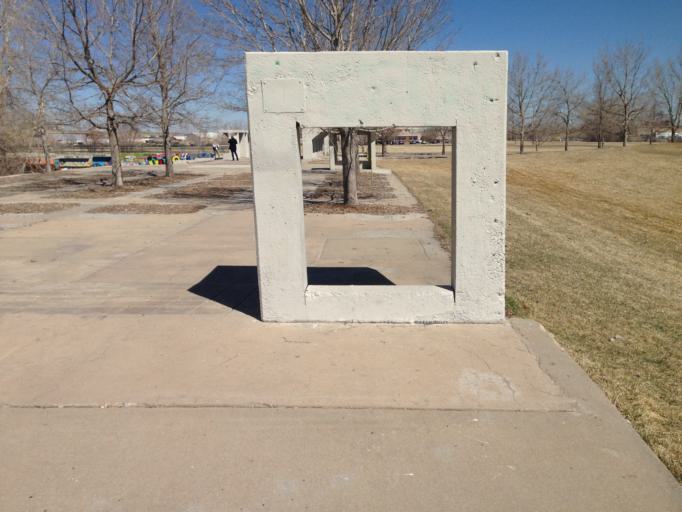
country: US
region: Colorado
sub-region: Adams County
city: Commerce City
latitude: 39.7892
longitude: -104.9732
